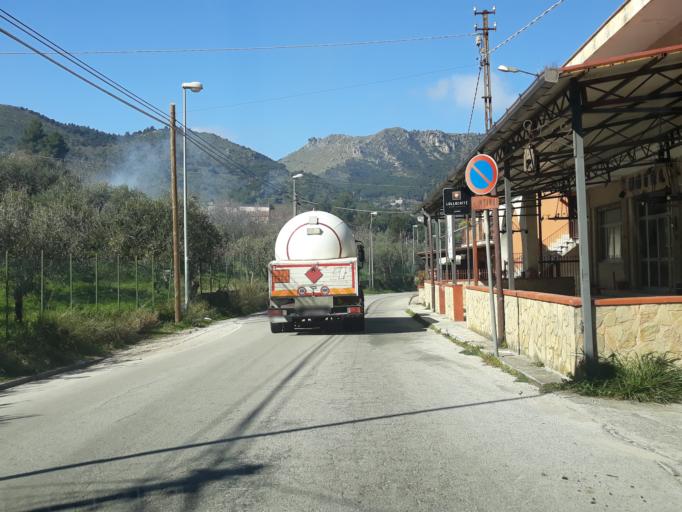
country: IT
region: Sicily
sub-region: Palermo
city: Piano dei Geli
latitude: 38.0851
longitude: 13.2645
